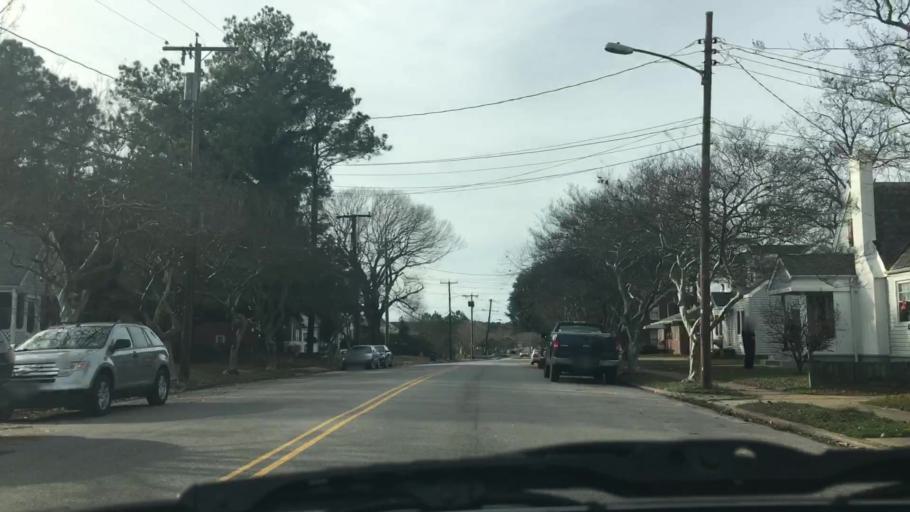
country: US
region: Virginia
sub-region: City of Norfolk
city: Norfolk
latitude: 36.8901
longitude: -76.2513
